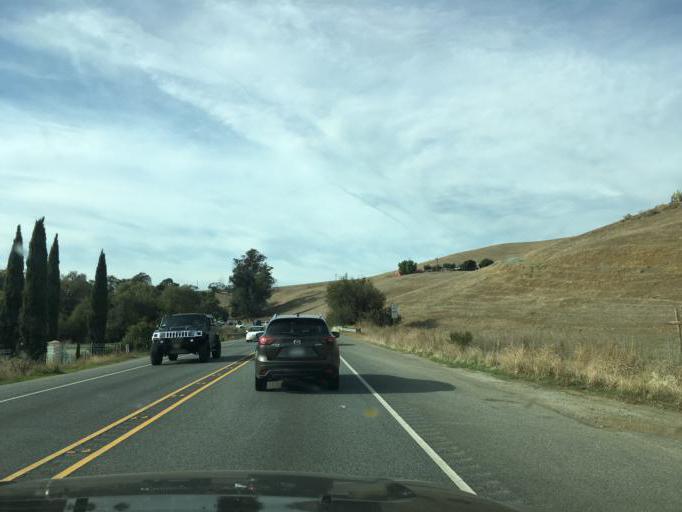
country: US
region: California
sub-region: San Benito County
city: Hollister
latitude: 36.9725
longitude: -121.4235
